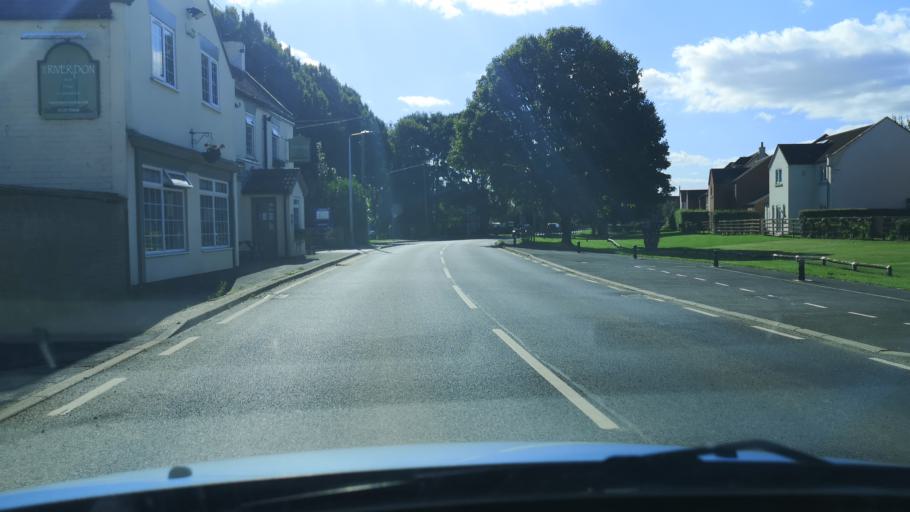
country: GB
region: England
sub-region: North Lincolnshire
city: Eastoft
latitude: 53.6360
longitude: -0.7849
